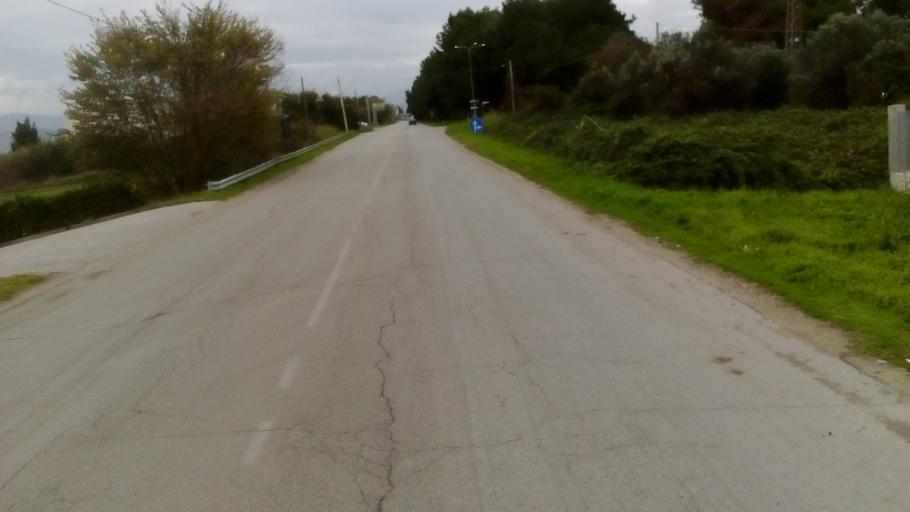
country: IT
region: Abruzzo
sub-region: Provincia di Chieti
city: San Salvo
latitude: 42.0425
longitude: 14.7527
